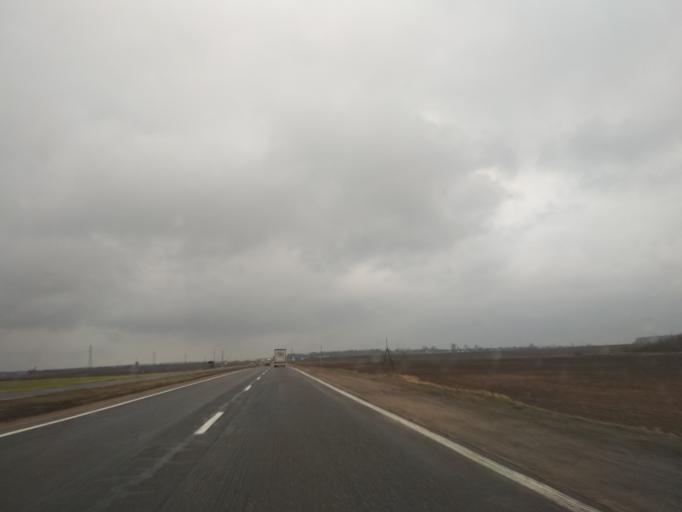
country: BY
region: Minsk
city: Dukora
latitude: 53.6447
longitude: 27.9871
